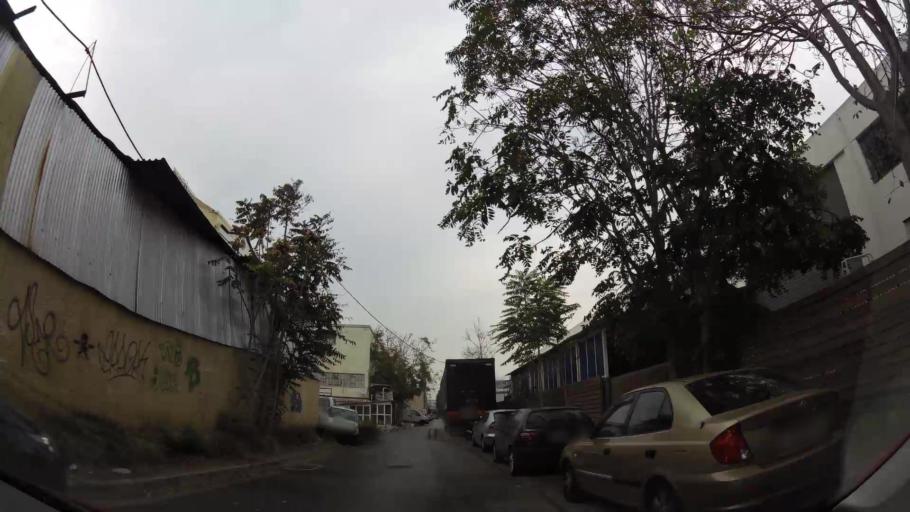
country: GR
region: Attica
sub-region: Nomarchia Athinas
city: Peristeri
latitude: 38.0013
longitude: 23.6989
